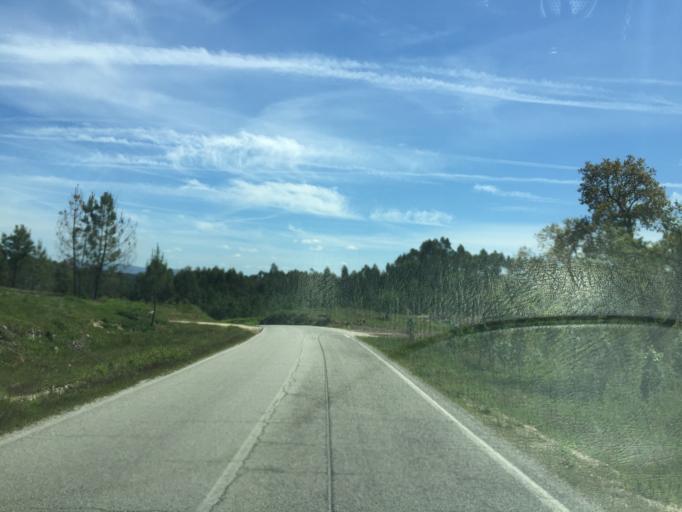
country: PT
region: Coimbra
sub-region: Soure
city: Soure
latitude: 40.0556
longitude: -8.6829
